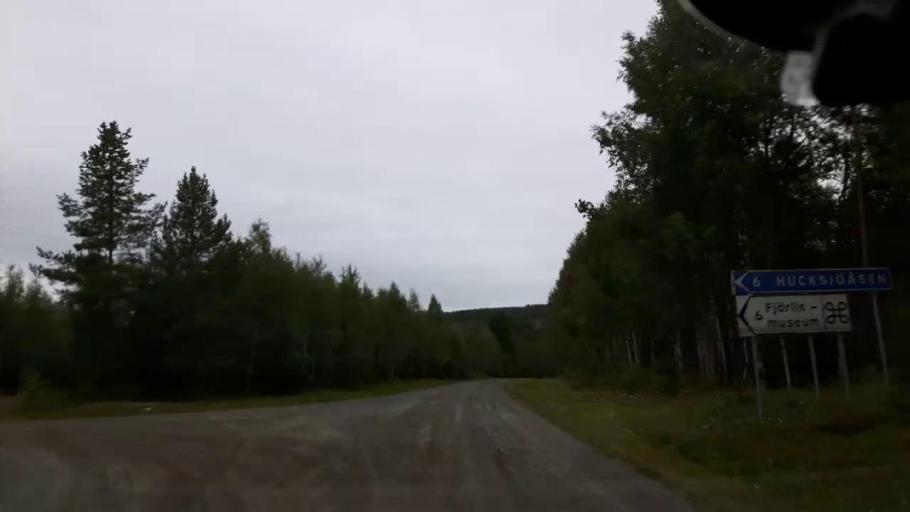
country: SE
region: Vaesternorrland
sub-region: Ange Kommun
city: Fransta
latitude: 62.8630
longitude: 15.9852
